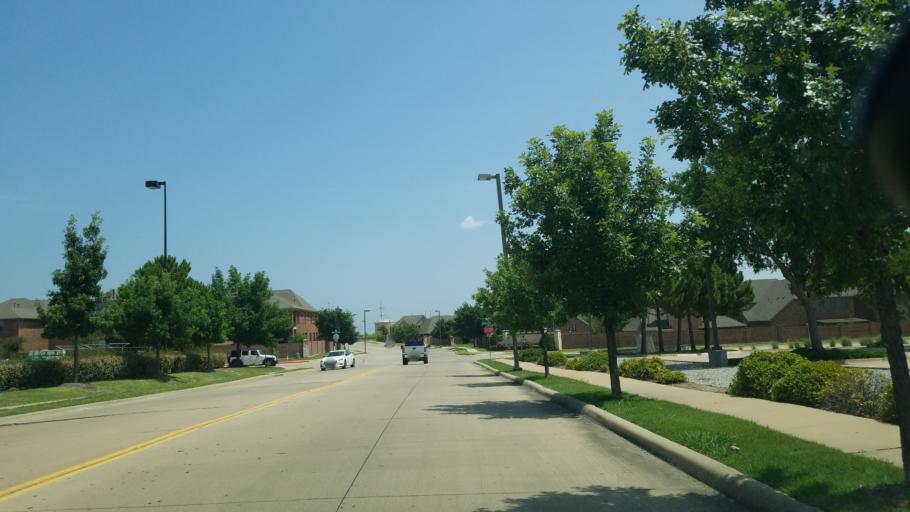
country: US
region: Texas
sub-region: Dallas County
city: Coppell
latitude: 32.9229
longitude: -96.9789
